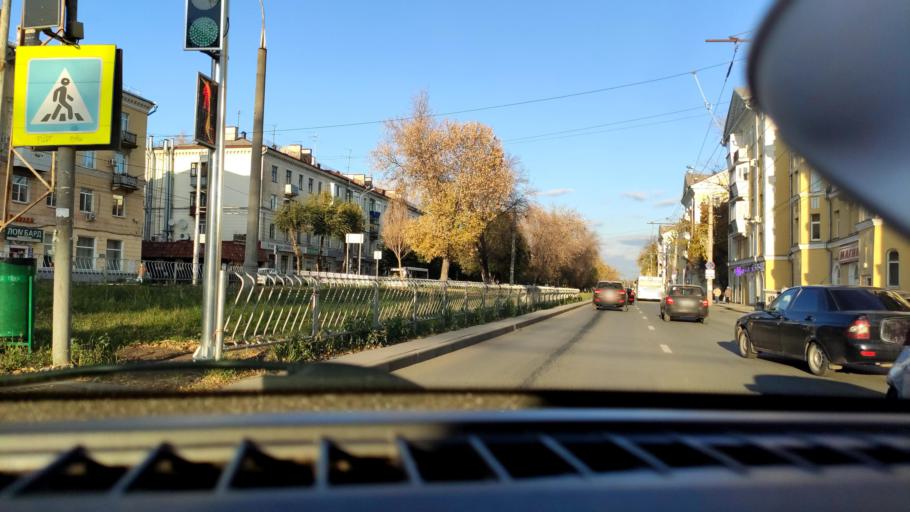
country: RU
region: Samara
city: Samara
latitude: 53.2161
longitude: 50.2561
